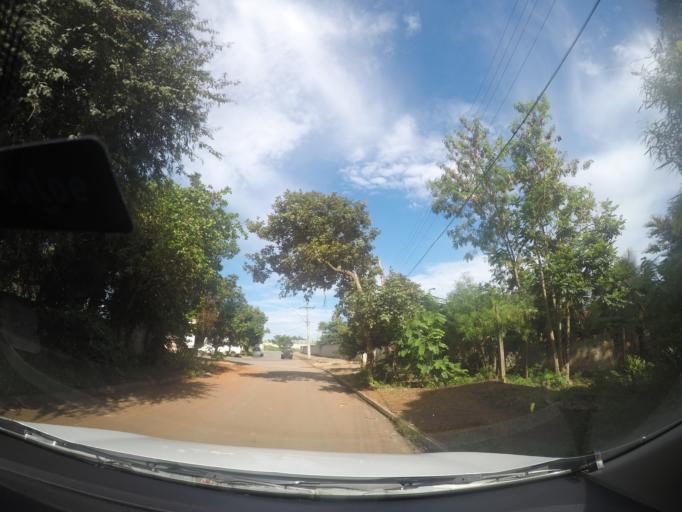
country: BR
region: Goias
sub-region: Goiania
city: Goiania
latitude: -16.6707
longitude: -49.1999
